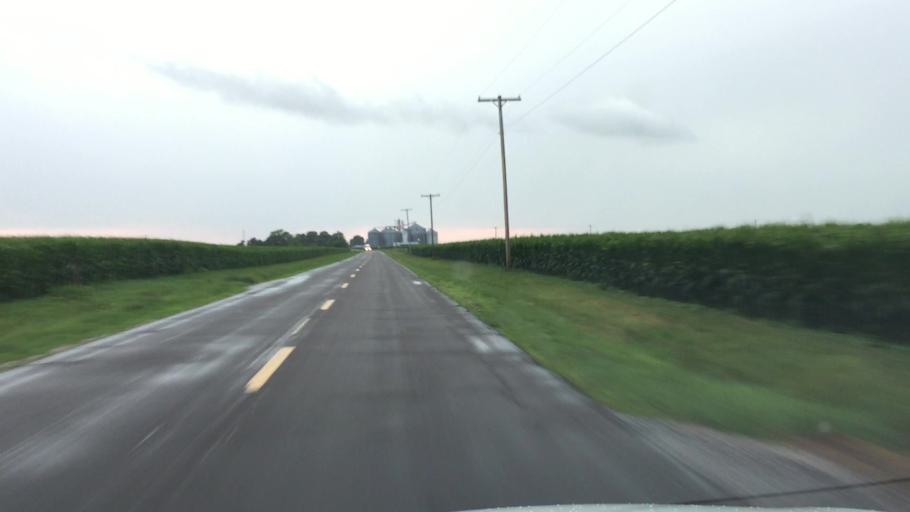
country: US
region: Illinois
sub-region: Hancock County
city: Carthage
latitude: 40.5205
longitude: -91.1525
